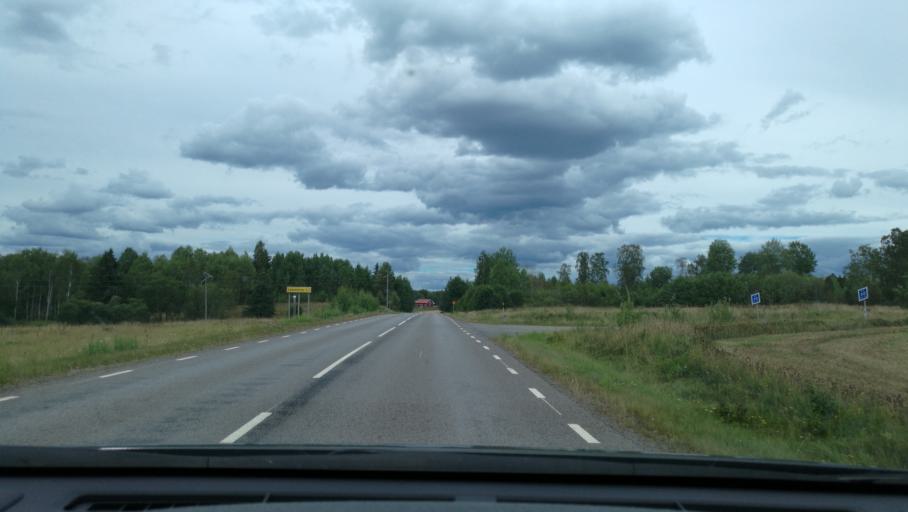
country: SE
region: OEstergoetland
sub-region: Norrkopings Kommun
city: Svartinge
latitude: 58.7111
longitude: 15.9343
